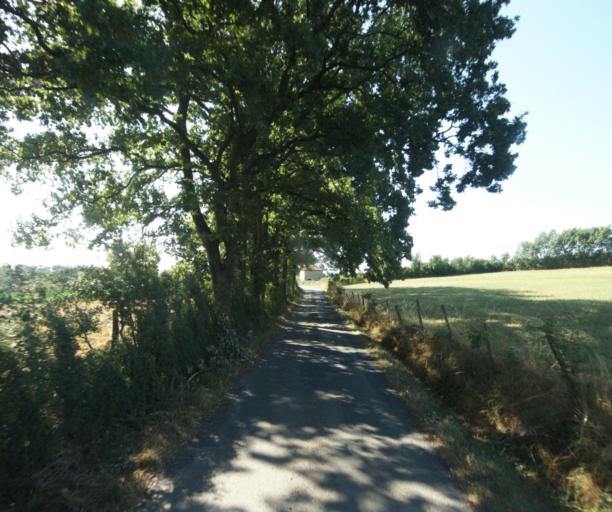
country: FR
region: Rhone-Alpes
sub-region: Departement du Rhone
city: Savigny
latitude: 45.8120
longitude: 4.5801
